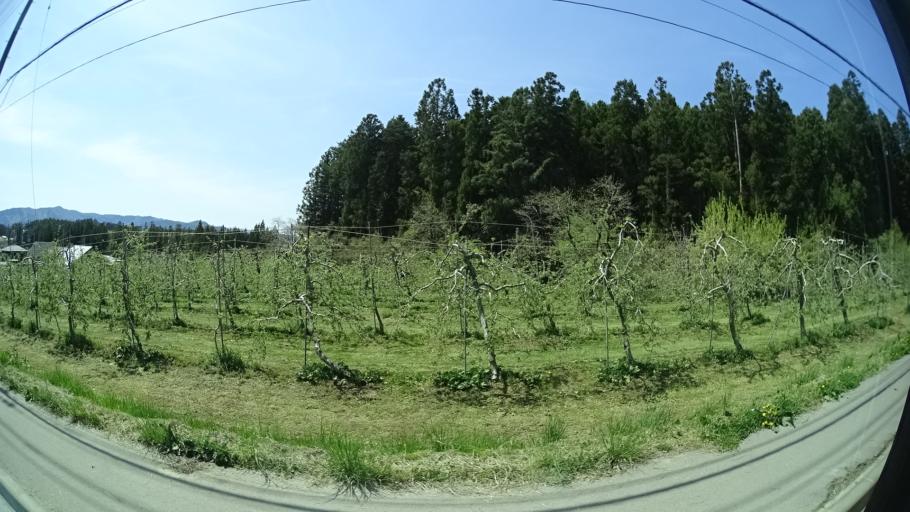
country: JP
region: Iwate
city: Ofunato
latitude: 39.0238
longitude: 141.6486
